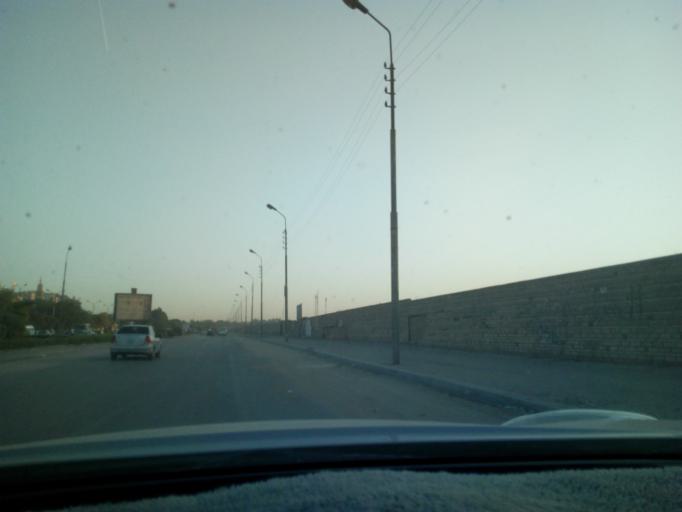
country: EG
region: Muhafazat al Qalyubiyah
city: Al Khankah
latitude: 30.1246
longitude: 31.3630
